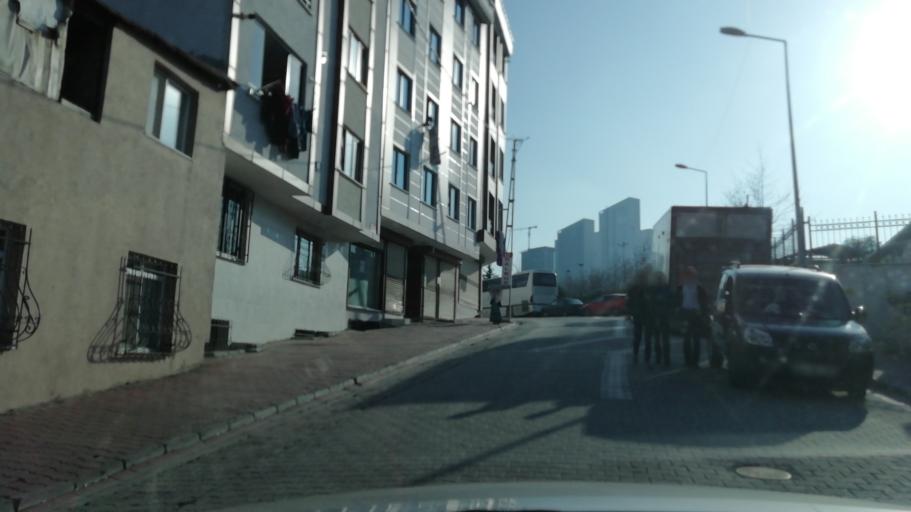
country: TR
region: Istanbul
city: Esenyurt
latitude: 41.0373
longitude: 28.6890
